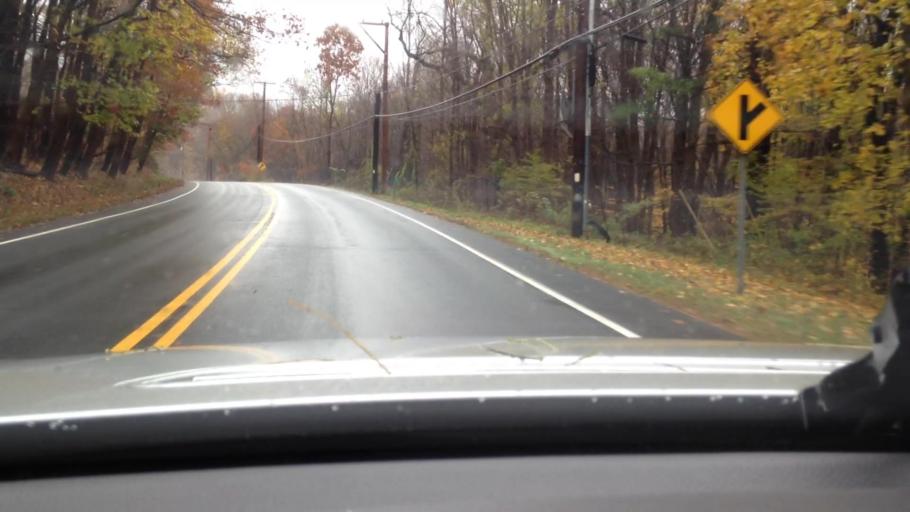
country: US
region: New York
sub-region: Putnam County
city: Cold Spring
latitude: 41.4123
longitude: -73.9376
